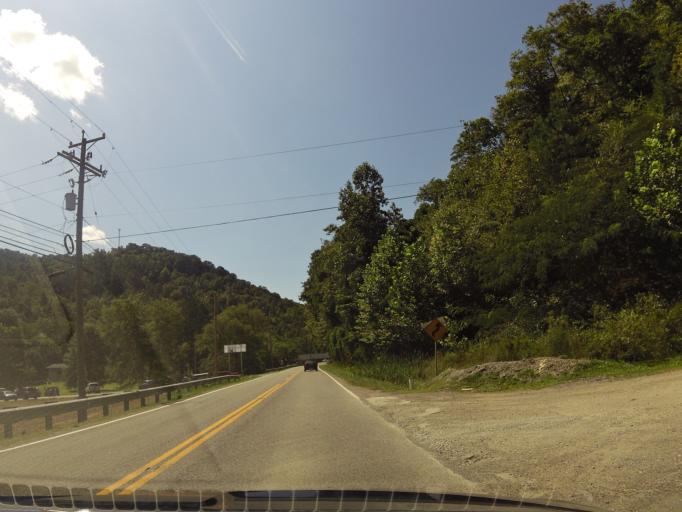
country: US
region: Kentucky
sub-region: Leslie County
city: Hyden
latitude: 37.1521
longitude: -83.3729
